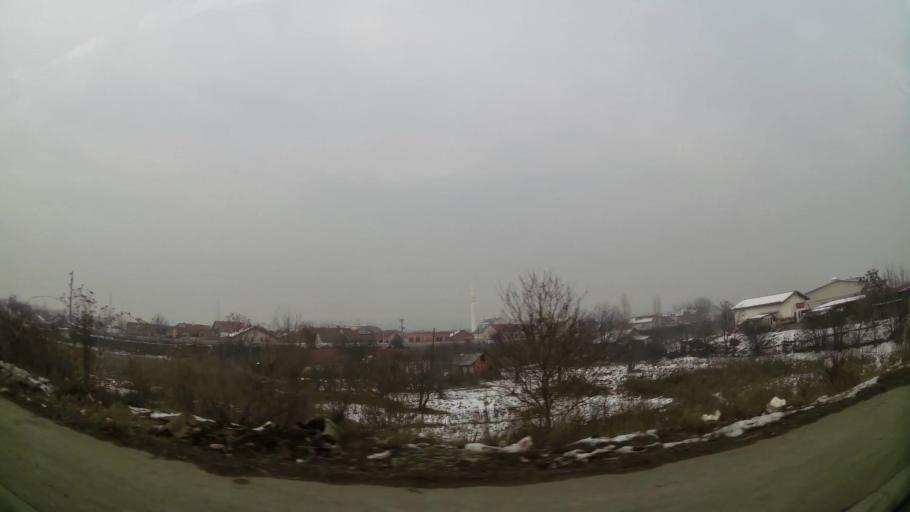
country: MK
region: Suto Orizari
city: Suto Orizare
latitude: 42.0267
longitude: 21.4243
